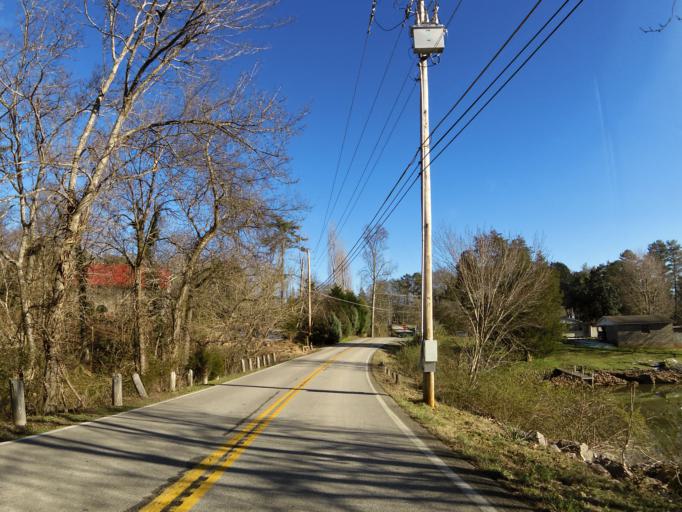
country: US
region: Tennessee
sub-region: Blount County
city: Louisville
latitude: 35.8903
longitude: -83.9890
